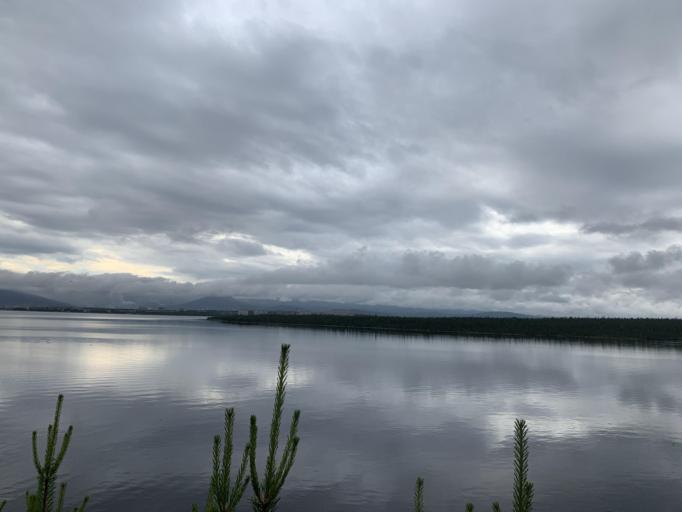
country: RU
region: Murmansk
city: Monchegorsk
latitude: 67.9503
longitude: 33.0217
